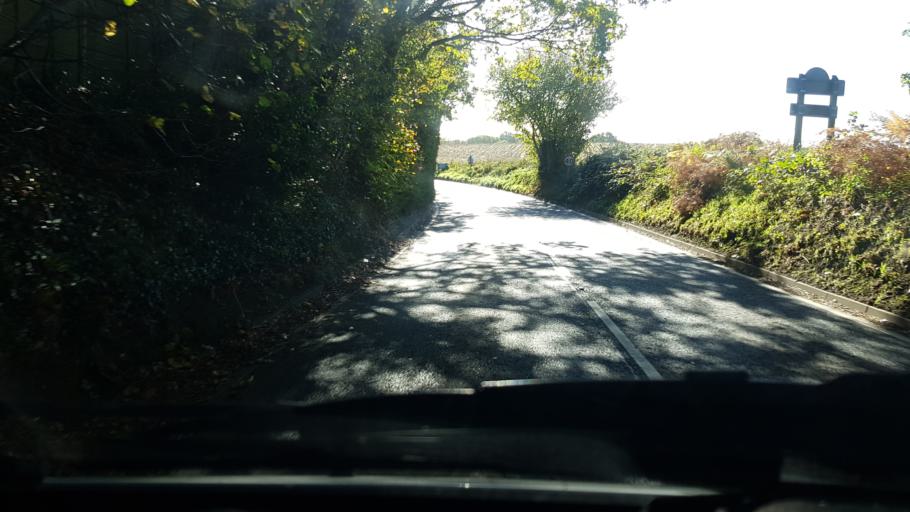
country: GB
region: England
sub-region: Surrey
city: Chilworth
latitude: 51.1795
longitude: -0.5229
